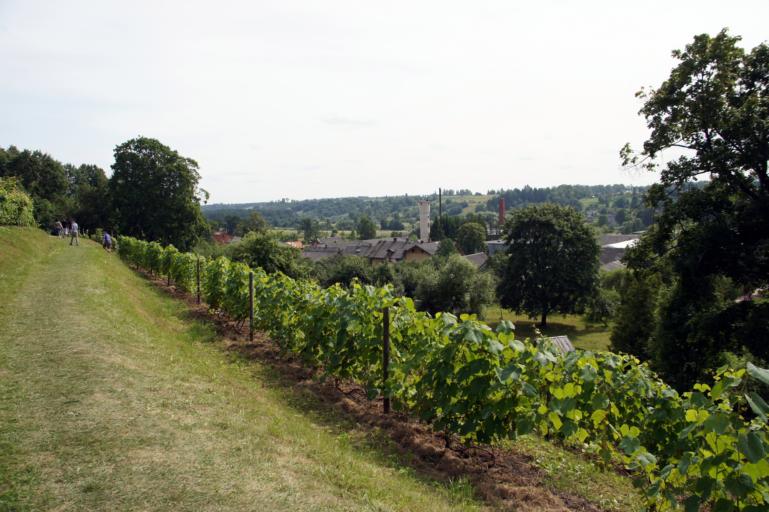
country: LV
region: Talsu Rajons
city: Sabile
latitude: 57.0460
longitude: 22.5766
